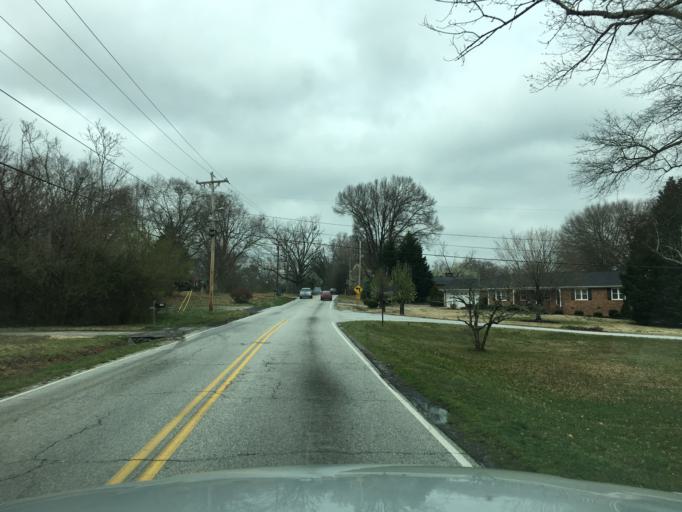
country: US
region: South Carolina
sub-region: Greenville County
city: Wade Hampton
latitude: 34.8822
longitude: -82.3298
